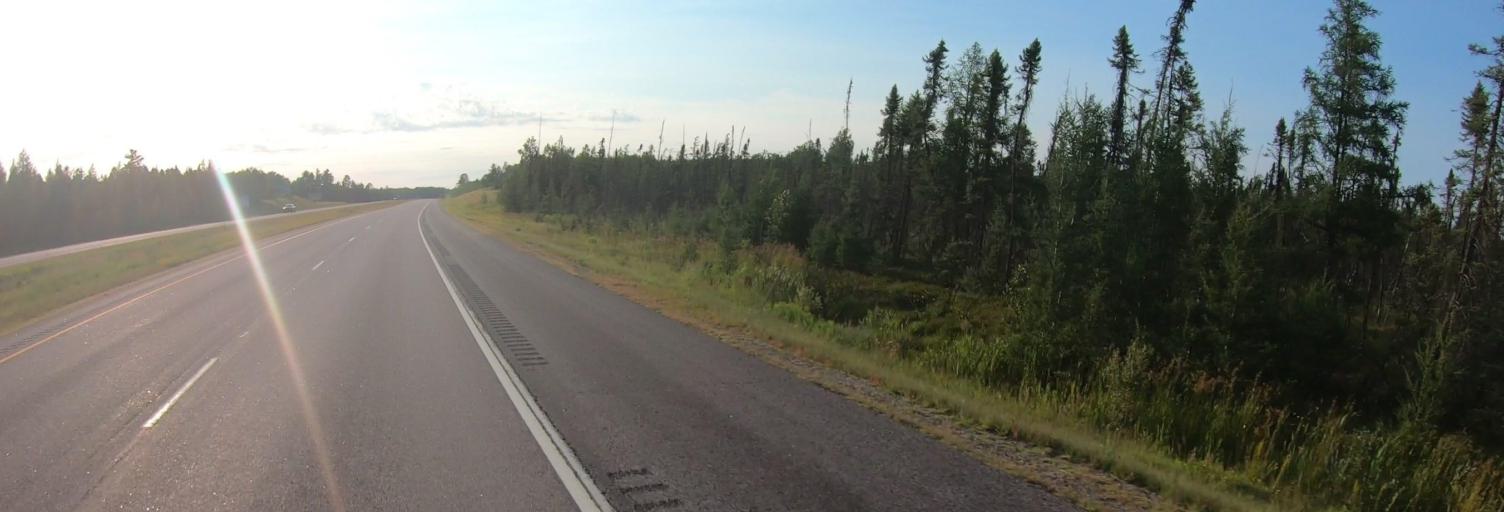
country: US
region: Minnesota
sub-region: Saint Louis County
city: Mountain Iron
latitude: 47.6614
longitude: -92.6240
